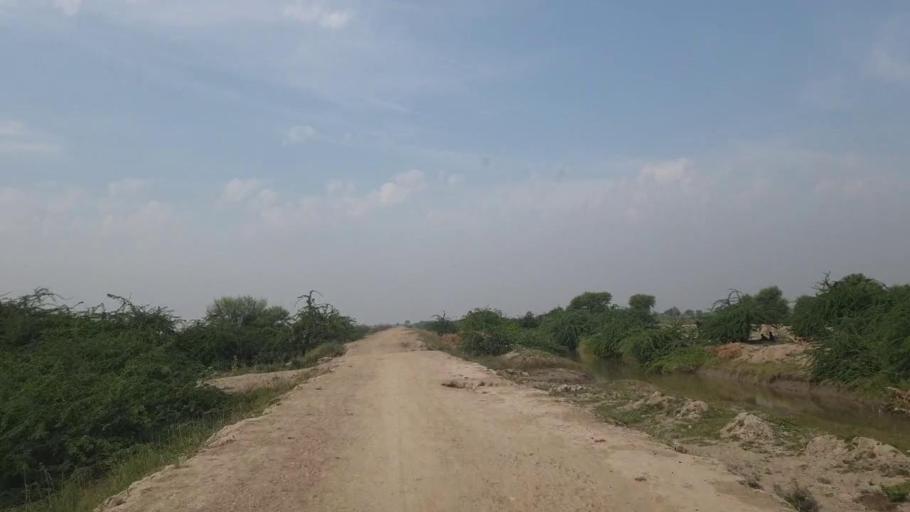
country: PK
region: Sindh
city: Rajo Khanani
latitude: 24.9610
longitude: 69.0215
